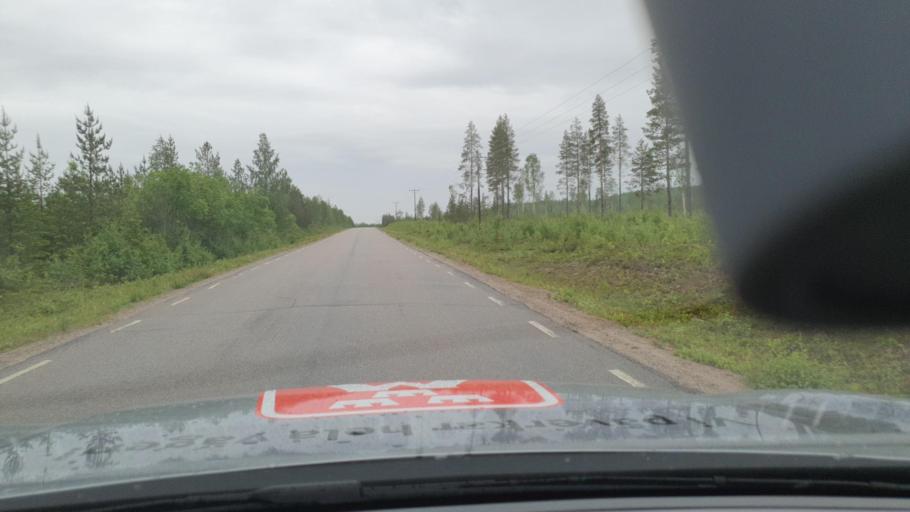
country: SE
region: Norrbotten
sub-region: Pajala Kommun
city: Pajala
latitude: 66.7593
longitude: 23.1556
